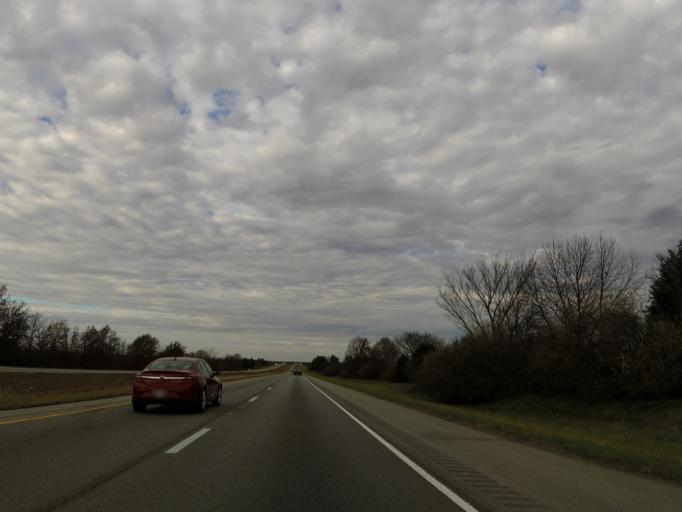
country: US
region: Illinois
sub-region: Jefferson County
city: Mount Vernon
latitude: 38.3622
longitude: -89.0574
